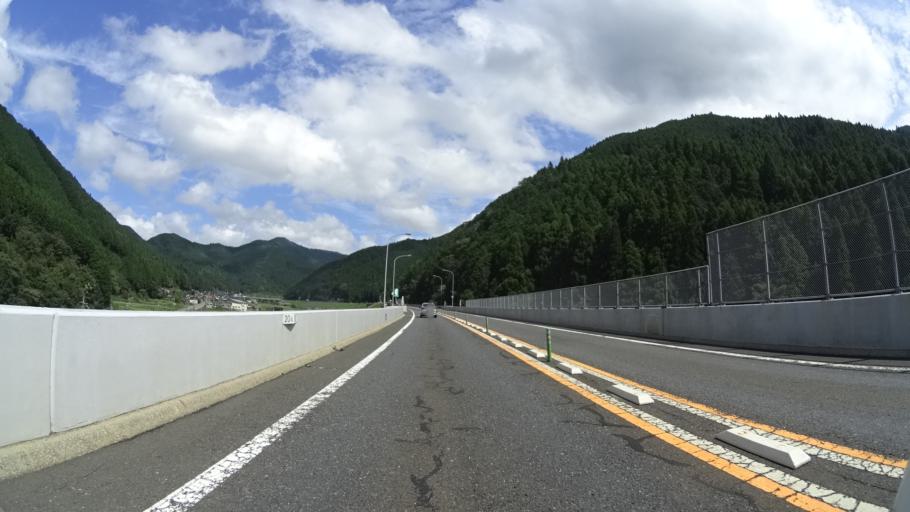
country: JP
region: Hyogo
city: Yamazakicho-nakabirose
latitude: 35.1945
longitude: 134.3358
